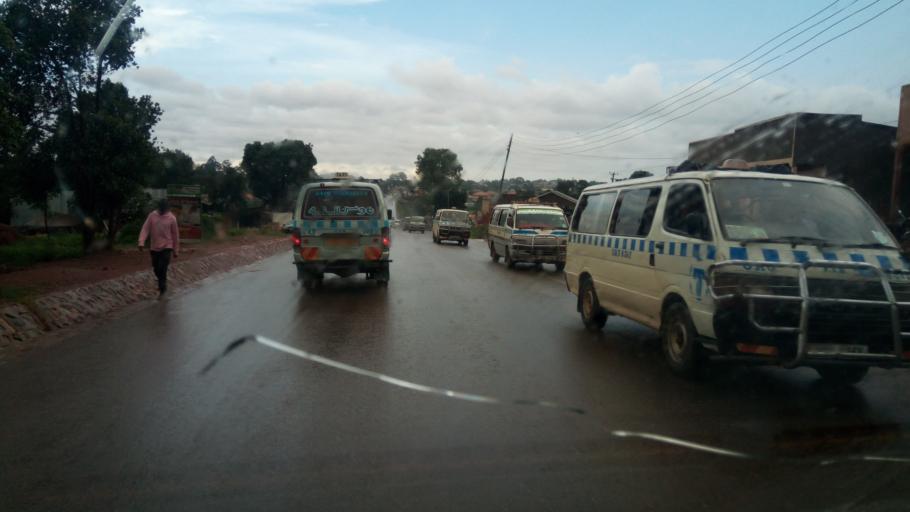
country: UG
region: Central Region
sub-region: Wakiso District
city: Wakiso
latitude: 0.3898
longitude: 32.5081
